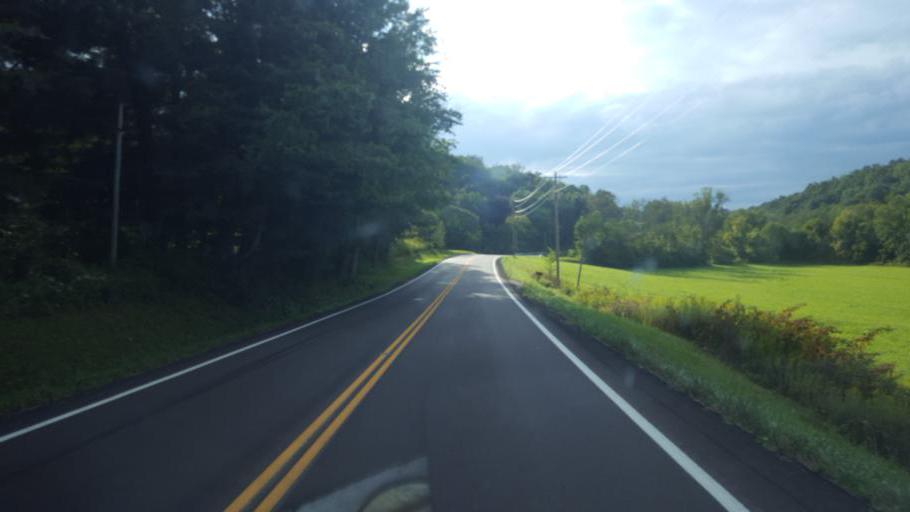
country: US
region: Ohio
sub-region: Knox County
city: Oak Hill
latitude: 40.4607
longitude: -82.1060
